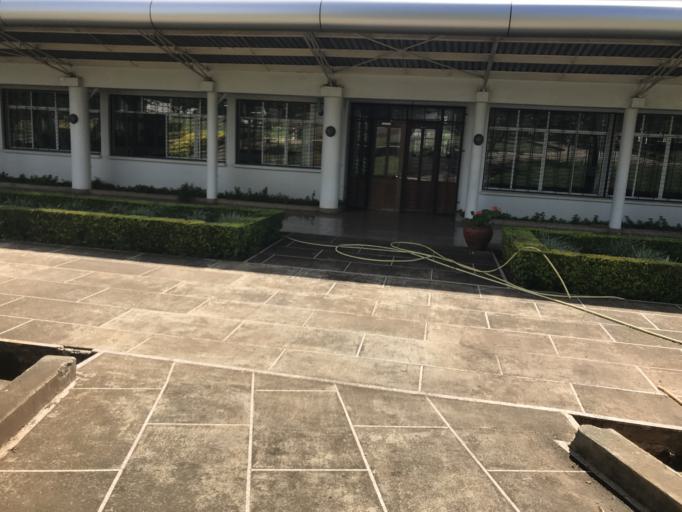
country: TZ
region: Arusha
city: Usa River
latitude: -3.4008
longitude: 36.7956
